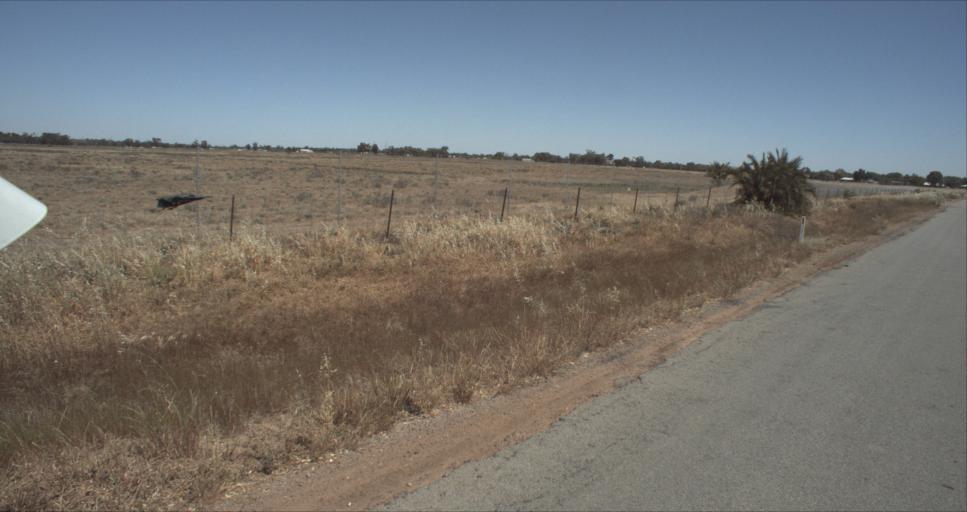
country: AU
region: New South Wales
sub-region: Leeton
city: Leeton
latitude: -34.5443
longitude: 146.4277
